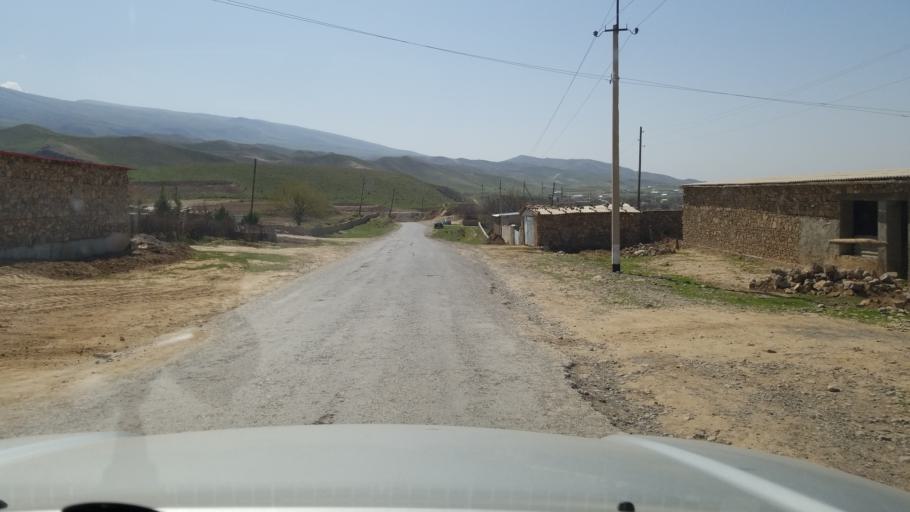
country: TM
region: Lebap
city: Gowurdak
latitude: 37.8898
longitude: 66.4612
